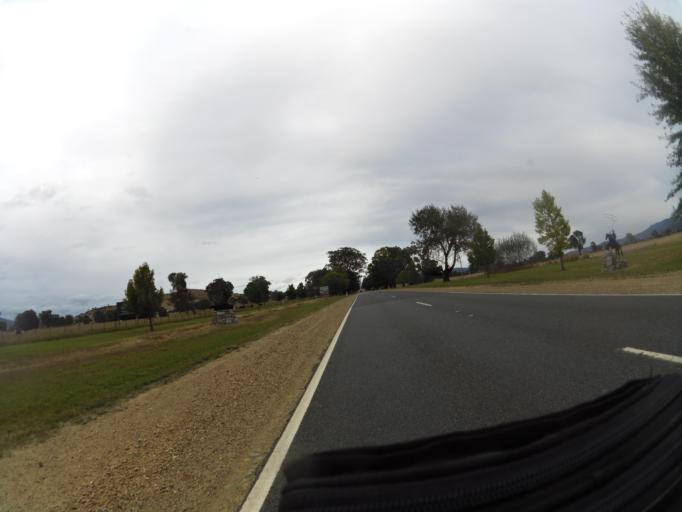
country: AU
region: New South Wales
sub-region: Snowy River
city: Jindabyne
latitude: -36.1820
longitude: 147.9238
